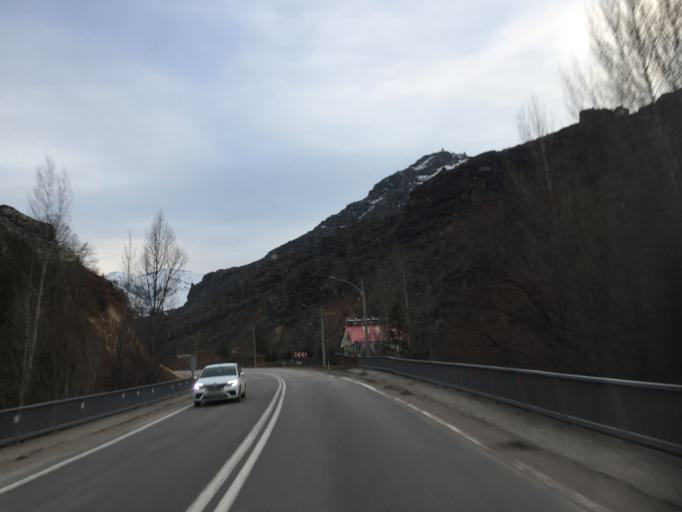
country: TR
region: Gumushane
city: Gumushkhane
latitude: 40.4786
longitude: 39.4617
